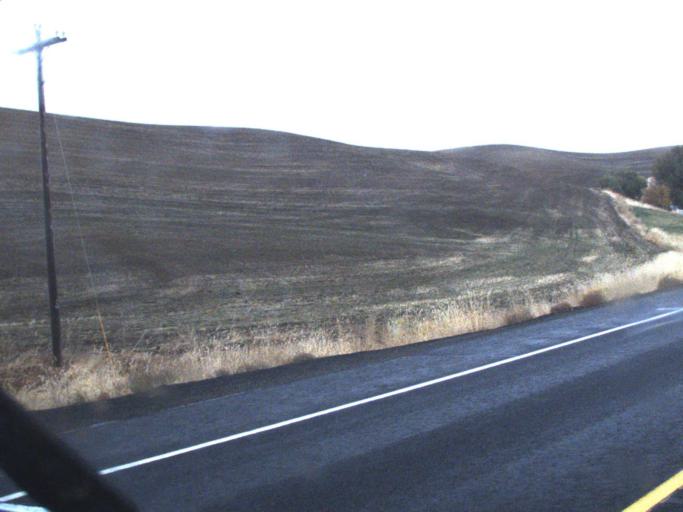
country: US
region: Washington
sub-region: Whitman County
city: Colfax
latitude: 46.9325
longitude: -117.3363
